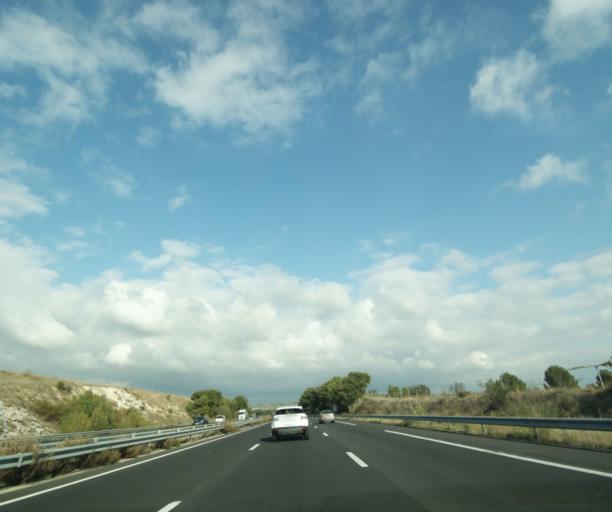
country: FR
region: Languedoc-Roussillon
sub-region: Departement de l'Aude
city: Fleury
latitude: 43.2377
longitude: 3.1422
